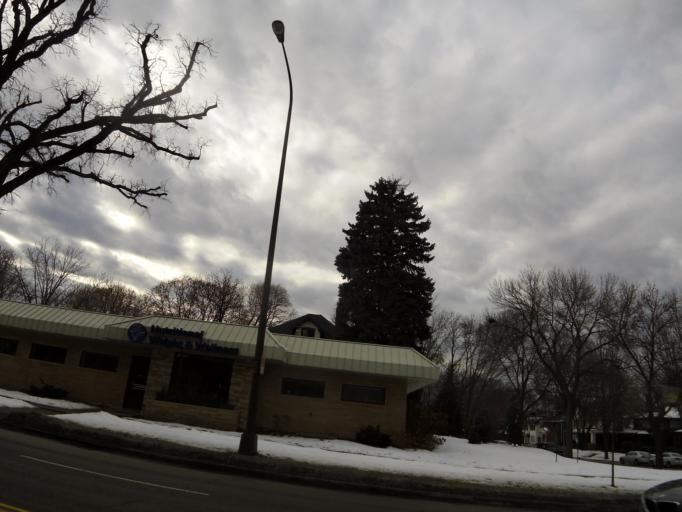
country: US
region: Minnesota
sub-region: Ramsey County
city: Falcon Heights
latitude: 44.9427
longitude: -93.1671
